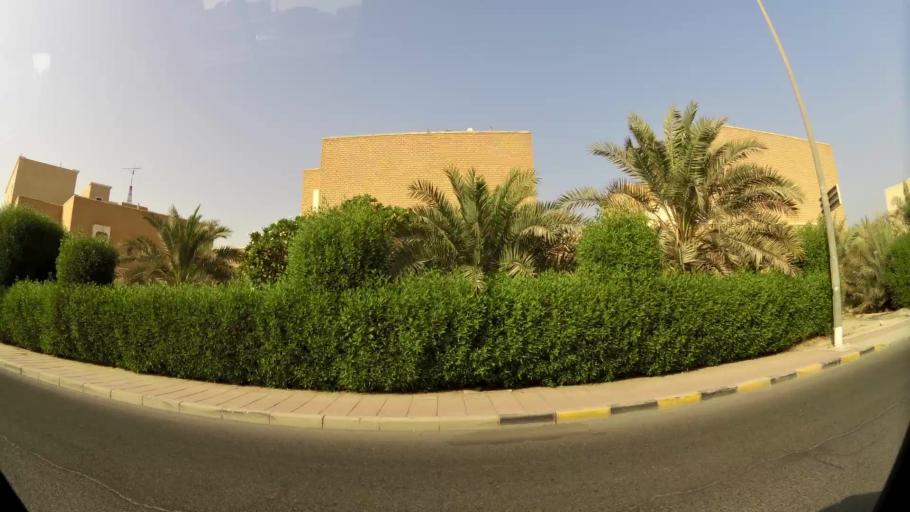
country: KW
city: Al Funaytis
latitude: 29.2156
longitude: 48.0818
